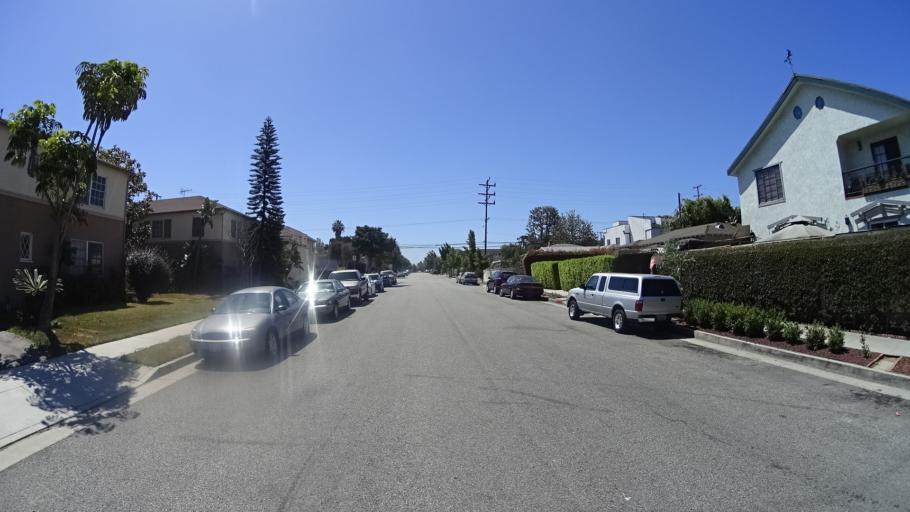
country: US
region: California
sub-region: Los Angeles County
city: Westwood, Los Angeles
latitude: 34.0256
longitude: -118.4527
